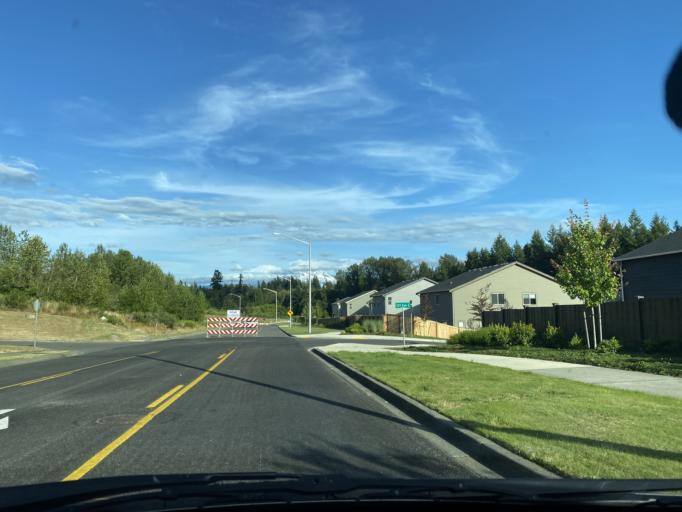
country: US
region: Washington
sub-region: Pierce County
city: Graham
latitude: 47.0868
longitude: -122.2582
